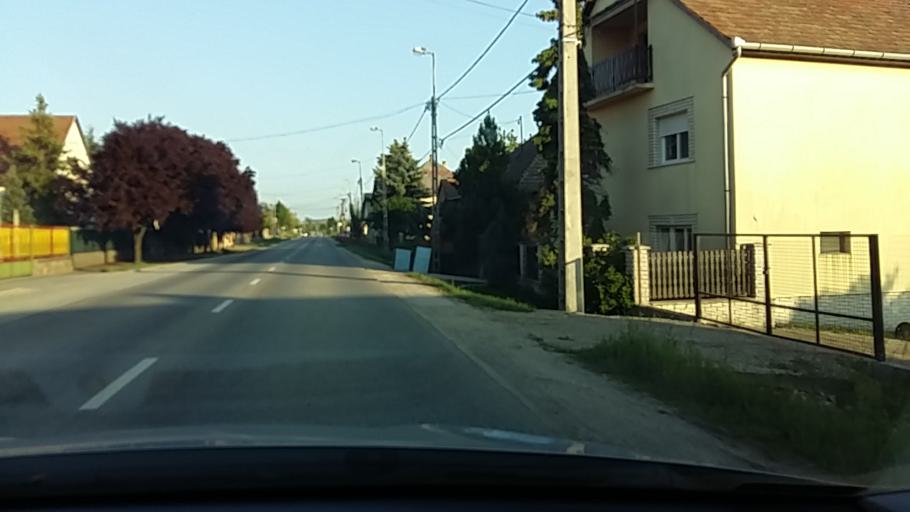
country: HU
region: Pest
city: Orbottyan
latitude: 47.6775
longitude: 19.2672
